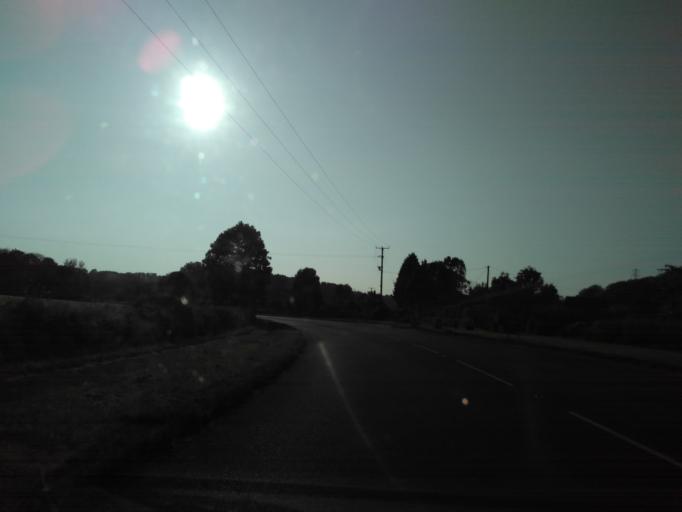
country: GB
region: England
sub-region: Kent
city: Dunkirk
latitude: 51.2460
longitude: 0.9678
